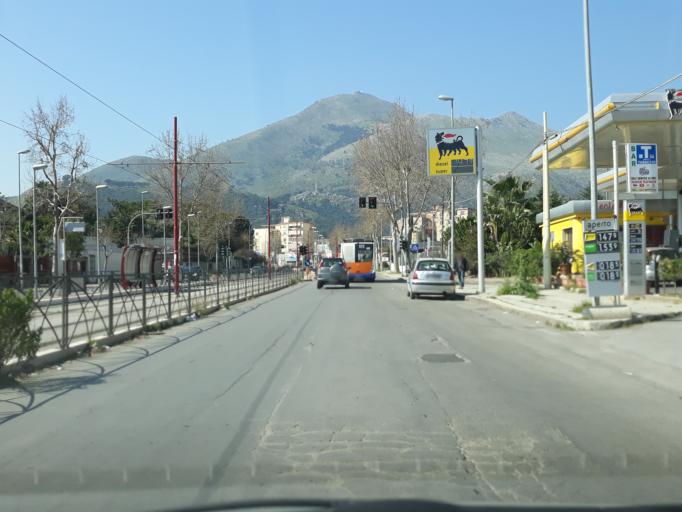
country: IT
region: Sicily
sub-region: Palermo
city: Palermo
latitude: 38.1316
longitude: 13.3057
